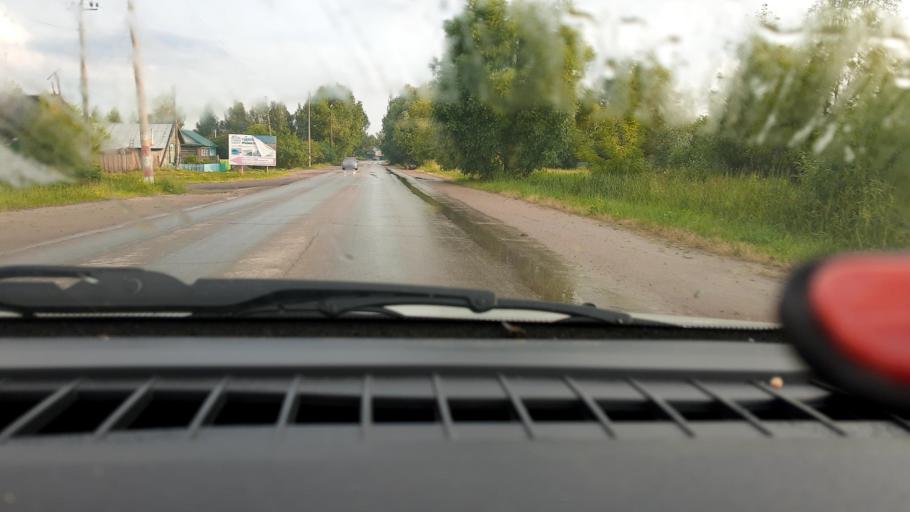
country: RU
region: Nizjnij Novgorod
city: Lukoyanov
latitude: 55.0400
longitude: 44.4965
